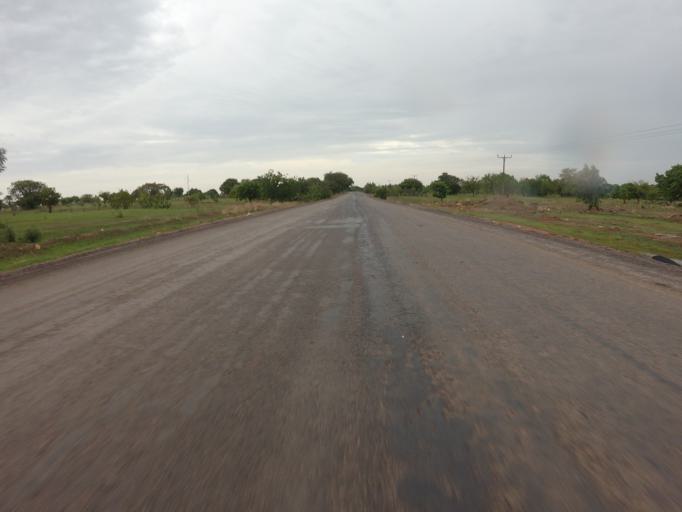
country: GH
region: Upper East
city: Bolgatanga
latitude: 10.8660
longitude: -0.6570
